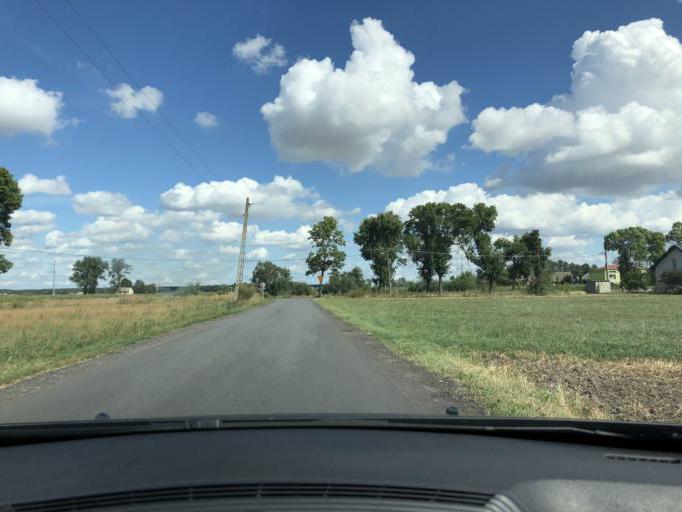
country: PL
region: Lodz Voivodeship
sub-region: Powiat wieruszowski
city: Czastary
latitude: 51.2411
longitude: 18.3591
